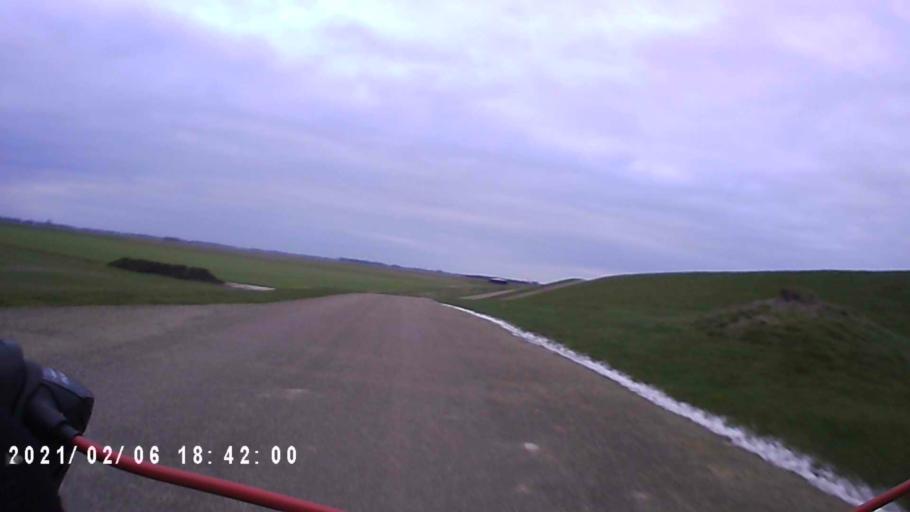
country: NL
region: Groningen
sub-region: Gemeente Winsum
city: Winsum
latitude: 53.4376
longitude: 6.6053
